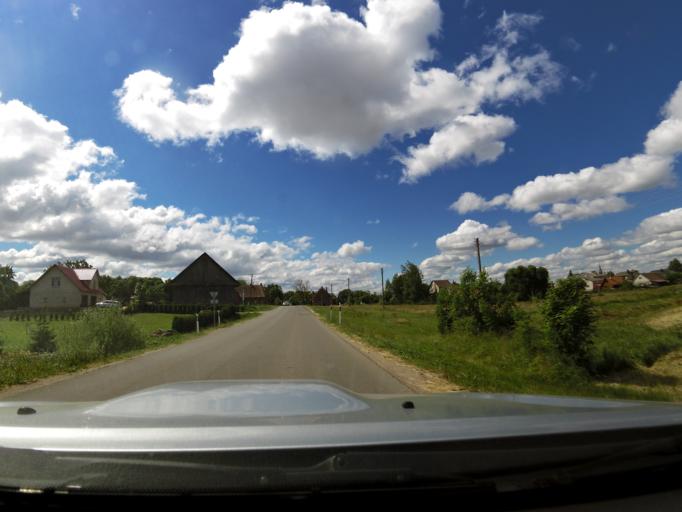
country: LT
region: Panevezys
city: Rokiskis
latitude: 55.9681
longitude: 25.5979
